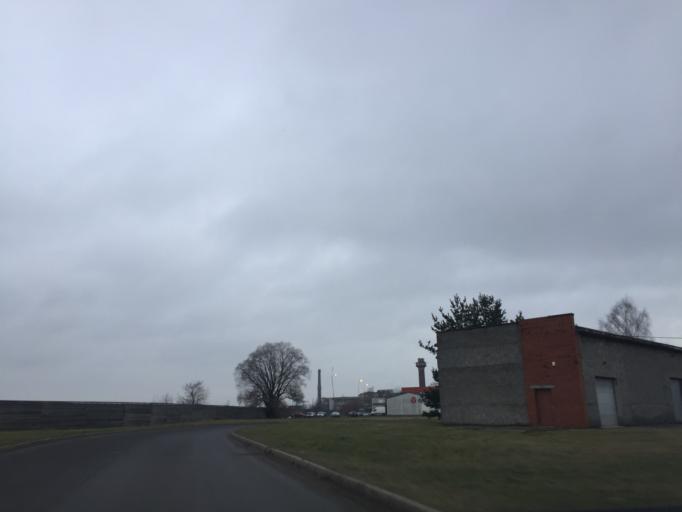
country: LV
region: Riga
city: Riga
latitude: 56.9906
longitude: 24.1128
